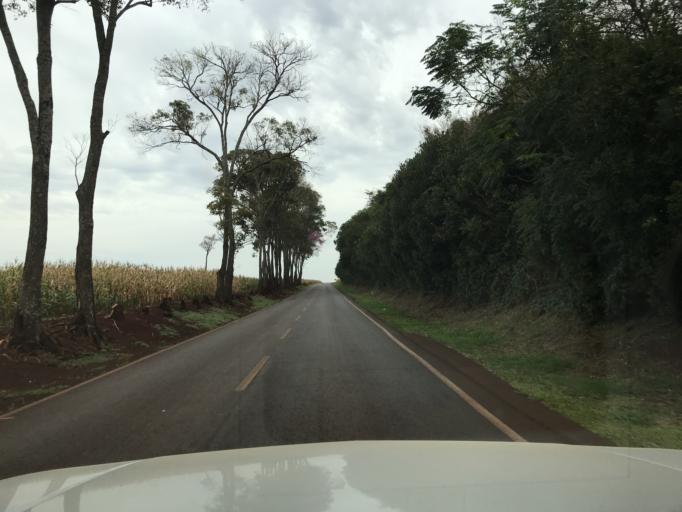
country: BR
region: Parana
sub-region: Palotina
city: Palotina
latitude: -24.4368
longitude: -53.9139
